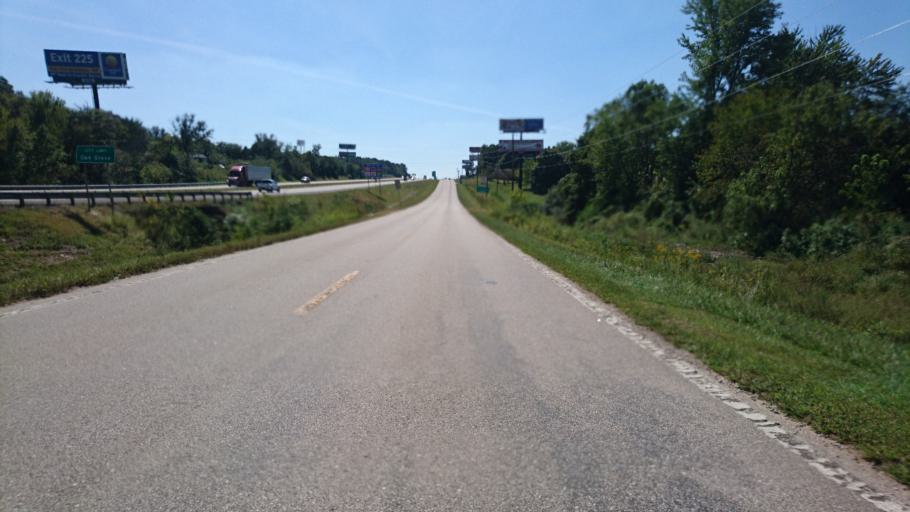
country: US
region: Missouri
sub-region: Franklin County
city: Sullivan
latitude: 38.2334
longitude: -91.1483
